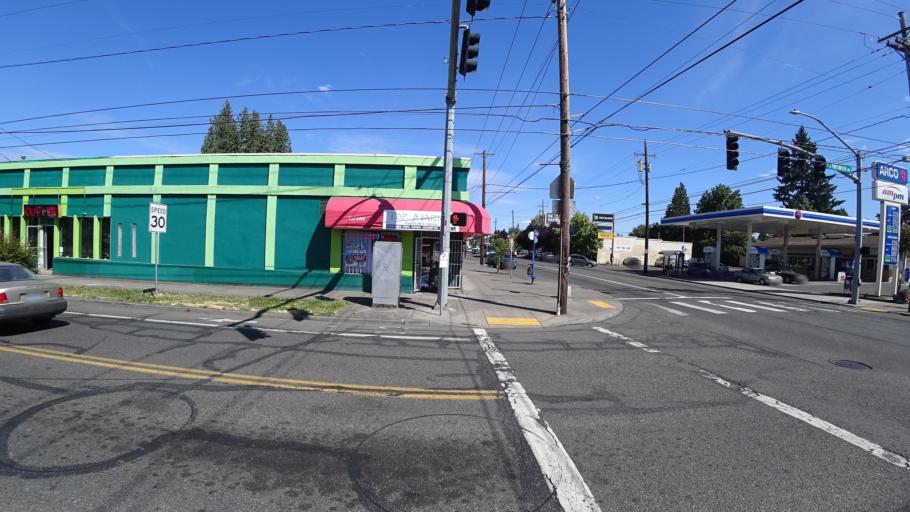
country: US
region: Oregon
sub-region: Multnomah County
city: Portland
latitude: 45.5826
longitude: -122.7240
